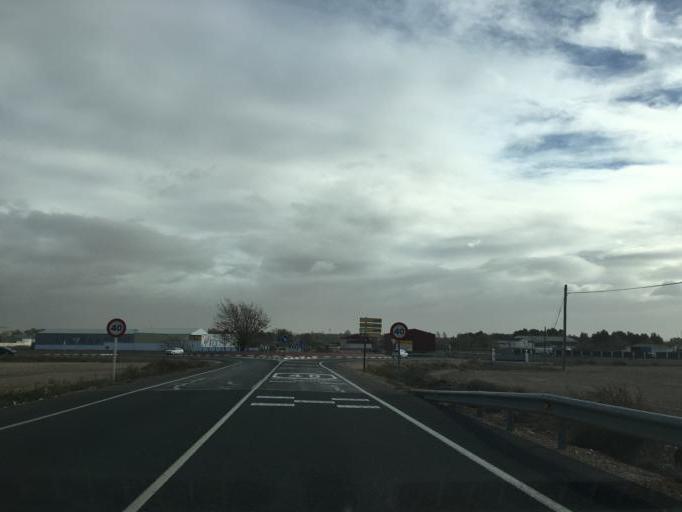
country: ES
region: Castille-La Mancha
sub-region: Provincia de Albacete
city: Albacete
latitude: 38.9988
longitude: -1.8964
